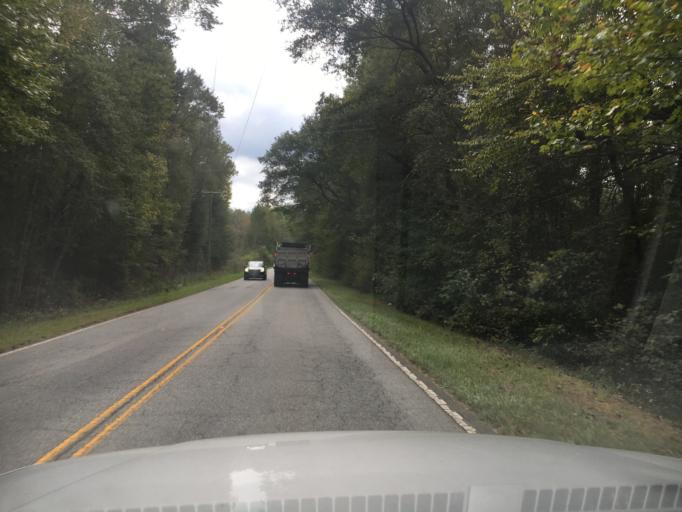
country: US
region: South Carolina
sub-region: Greenville County
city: Greer
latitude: 35.0247
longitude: -82.2669
